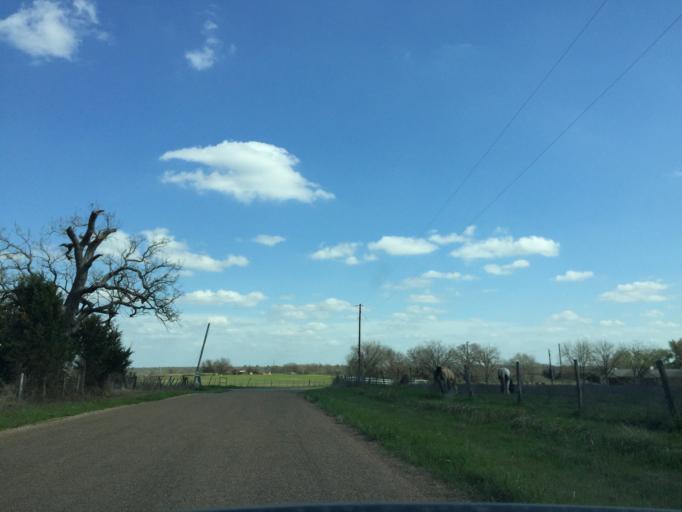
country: US
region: Texas
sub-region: Milam County
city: Thorndale
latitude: 30.5515
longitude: -97.1481
